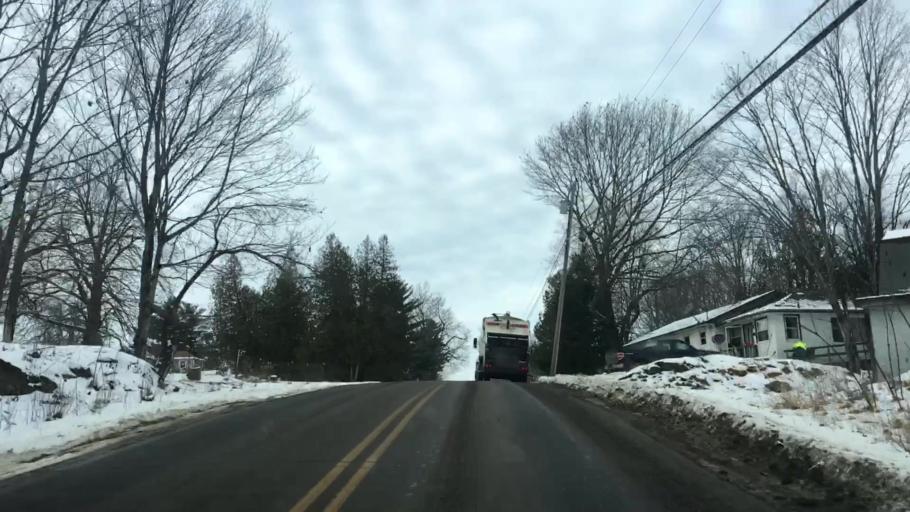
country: US
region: Maine
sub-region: Kennebec County
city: Chelsea
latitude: 44.2555
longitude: -69.6414
